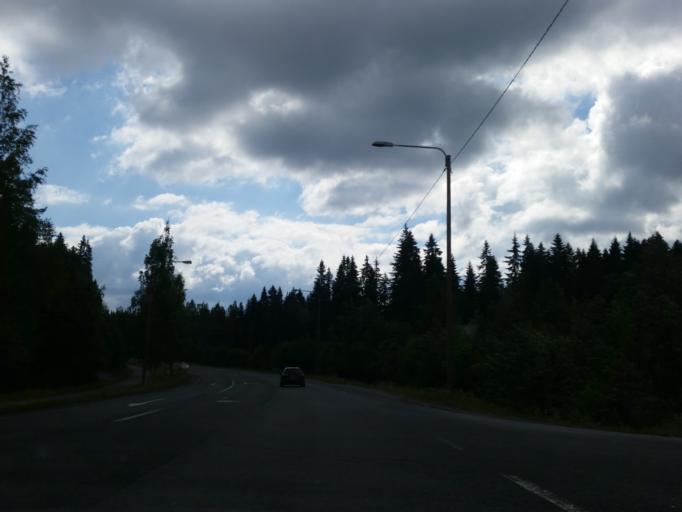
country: FI
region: Northern Savo
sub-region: Kuopio
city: Kuopio
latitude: 62.8387
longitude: 27.5629
